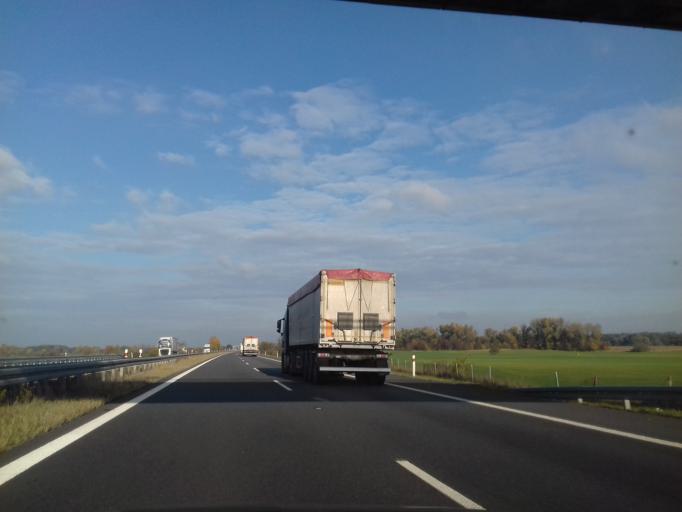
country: CZ
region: South Moravian
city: Kostice
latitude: 48.7649
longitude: 16.9431
